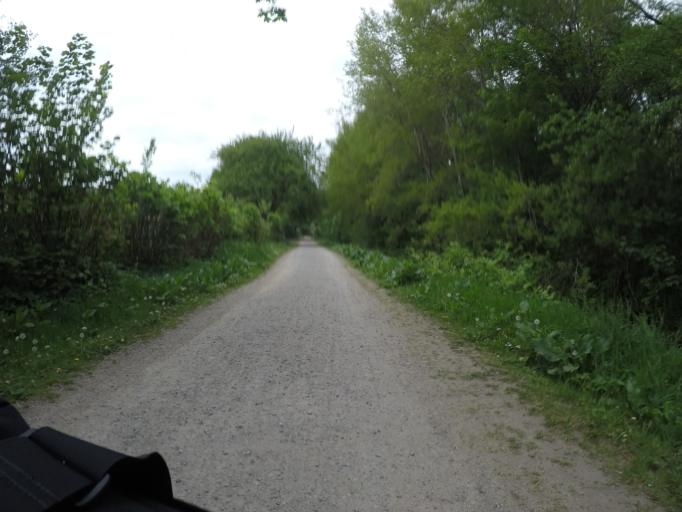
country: DE
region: Hamburg
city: Winterhude
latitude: 53.6297
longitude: 9.9797
